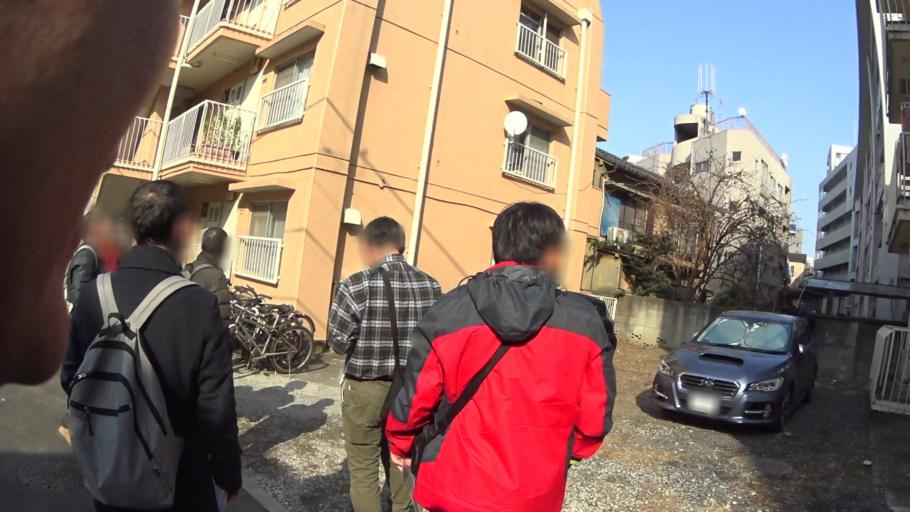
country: JP
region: Tokyo
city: Tokyo
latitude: 35.6417
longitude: 139.7178
